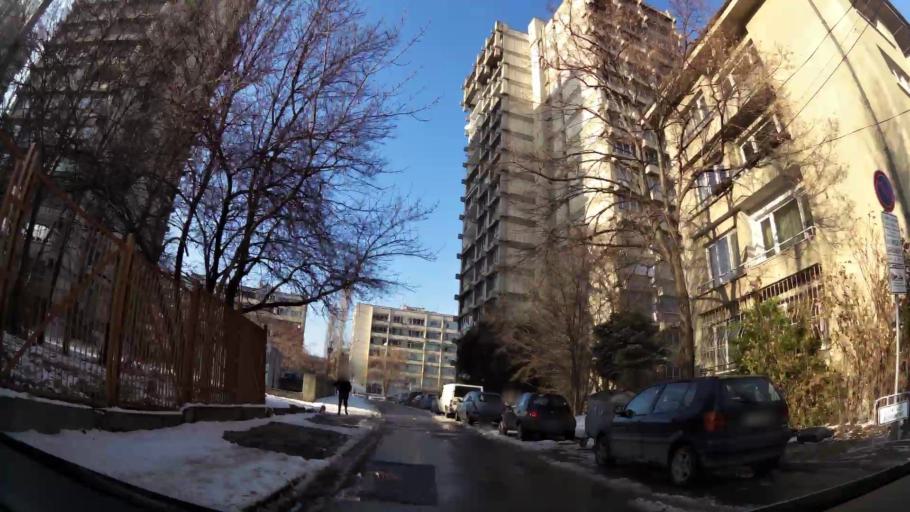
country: BG
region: Sofia-Capital
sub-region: Stolichna Obshtina
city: Sofia
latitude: 42.6718
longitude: 23.3535
